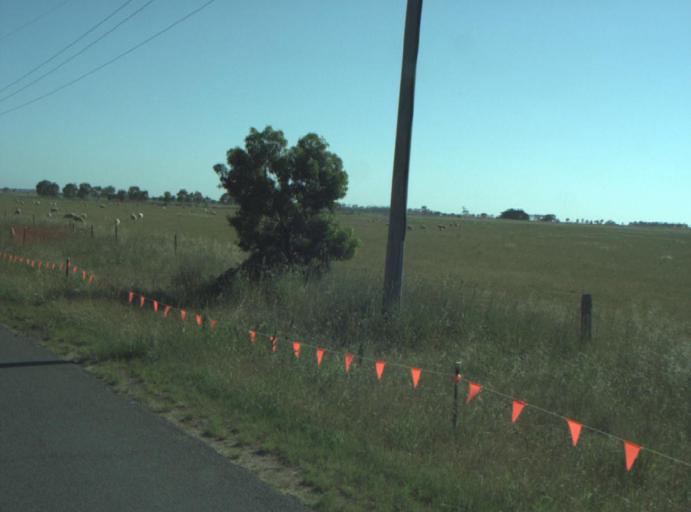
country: AU
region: Victoria
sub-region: Wyndham
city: Little River
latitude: -37.9762
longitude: 144.4607
